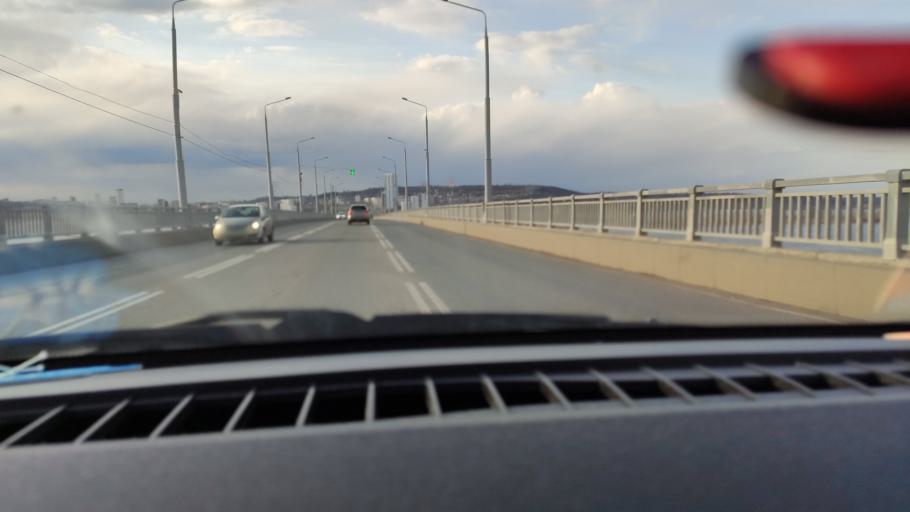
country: RU
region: Saratov
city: Engel's
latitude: 51.5130
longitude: 46.0735
